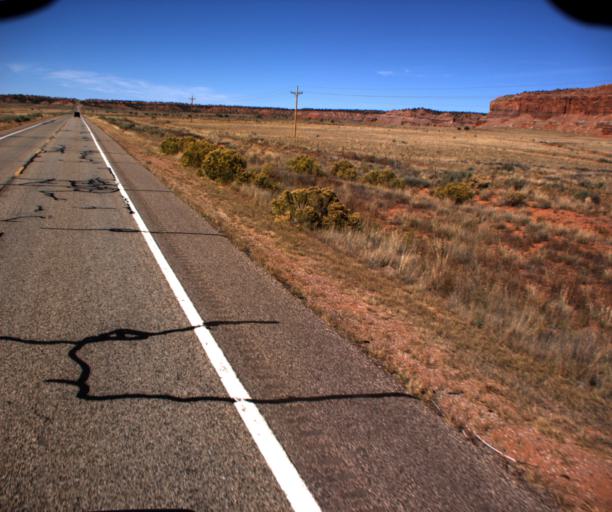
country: US
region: Arizona
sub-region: Mohave County
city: Colorado City
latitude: 36.8718
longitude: -112.8598
